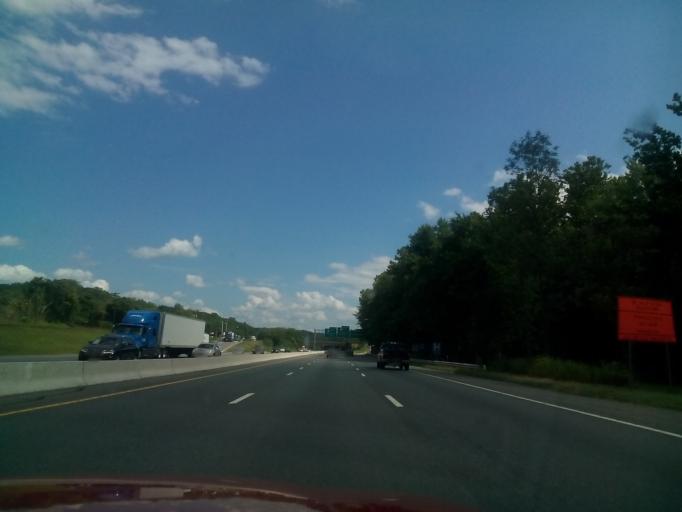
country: US
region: Pennsylvania
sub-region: Northampton County
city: East Bangor
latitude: 40.9331
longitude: -75.1014
